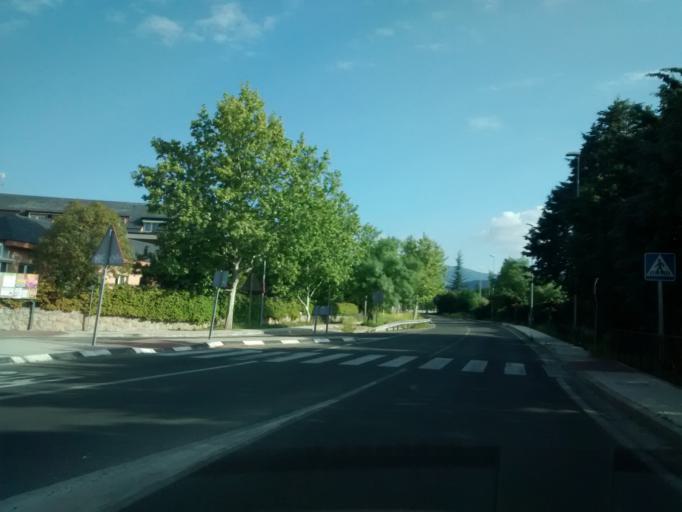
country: ES
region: Madrid
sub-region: Provincia de Madrid
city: Alpedrete
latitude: 40.6453
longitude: -4.0219
